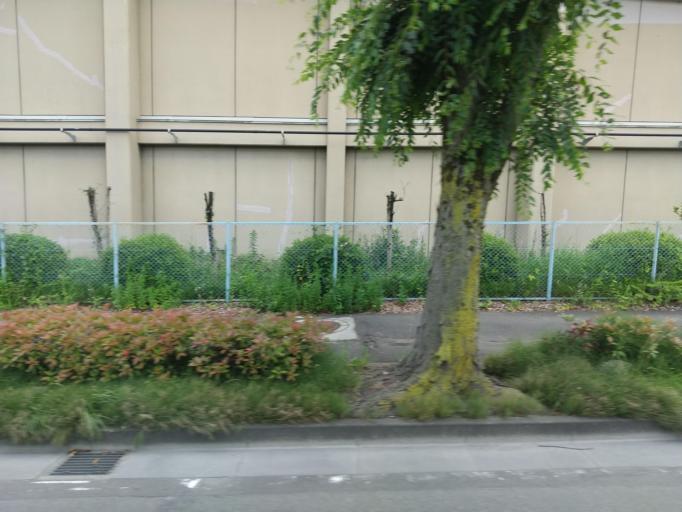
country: JP
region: Miyagi
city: Sendai-shi
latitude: 38.2610
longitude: 140.9293
